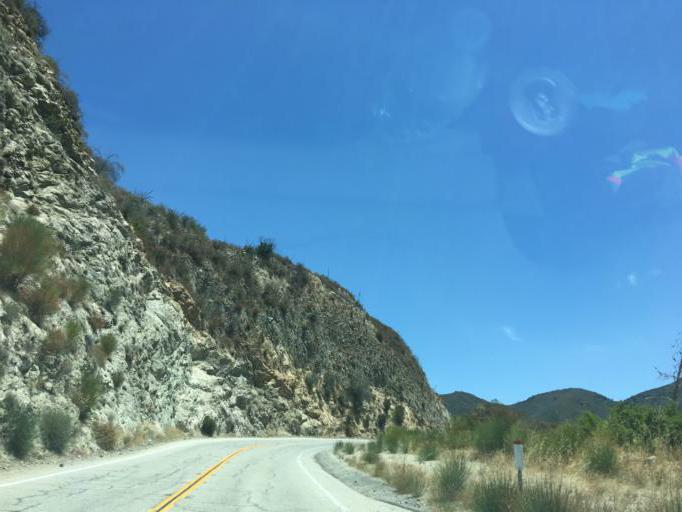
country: US
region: California
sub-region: Los Angeles County
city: La Crescenta-Montrose
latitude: 34.2813
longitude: -118.2159
